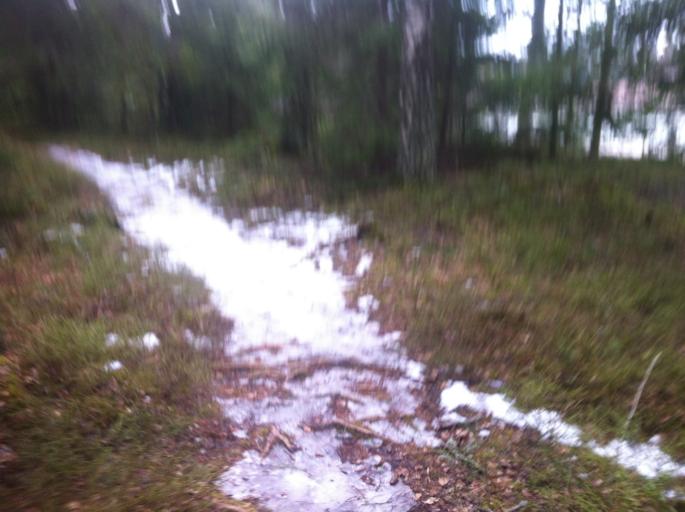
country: FI
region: Varsinais-Suomi
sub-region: Turku
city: Naantali
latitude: 60.4872
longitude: 22.0592
